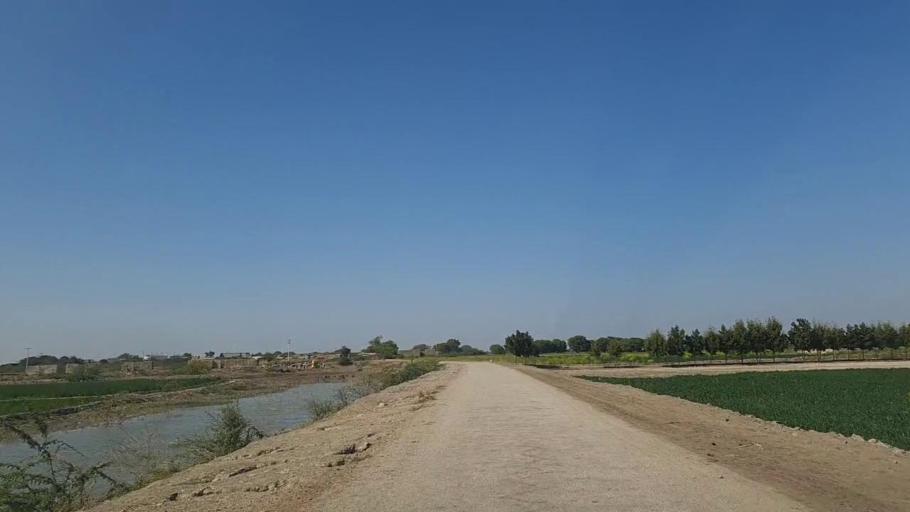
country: PK
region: Sindh
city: Naukot
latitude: 25.0018
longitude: 69.3379
